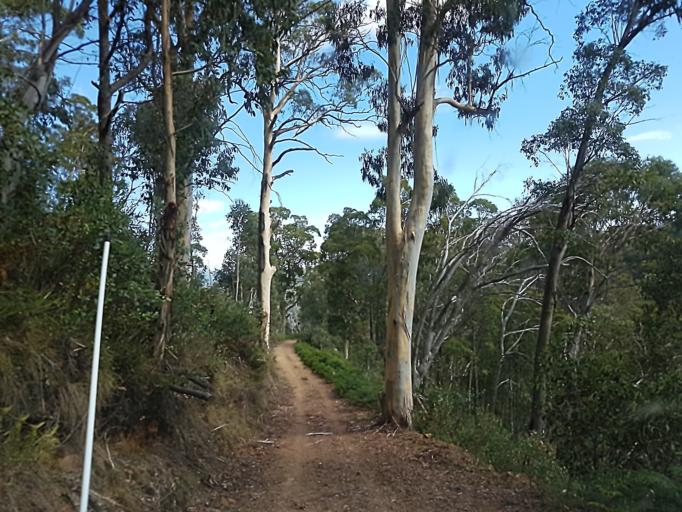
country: AU
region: Victoria
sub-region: Alpine
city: Mount Beauty
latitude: -36.9152
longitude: 146.9995
